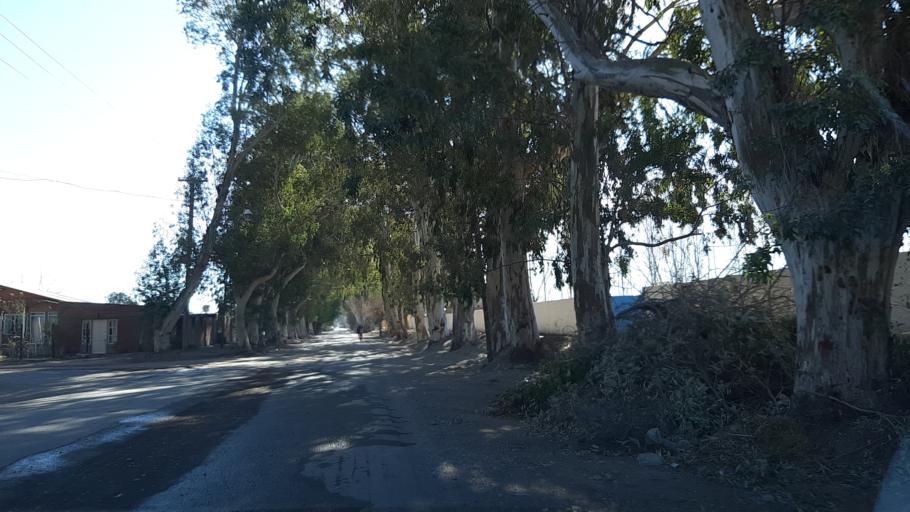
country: AR
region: San Juan
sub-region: Departamento de Zonda
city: Zonda
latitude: -31.5517
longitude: -68.7280
